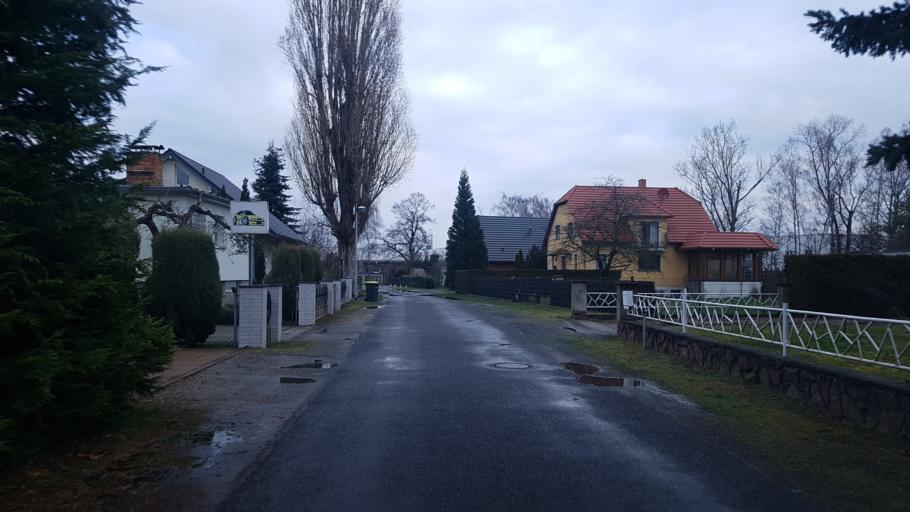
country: DE
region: Brandenburg
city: Elsterwerda
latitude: 51.4631
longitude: 13.5331
